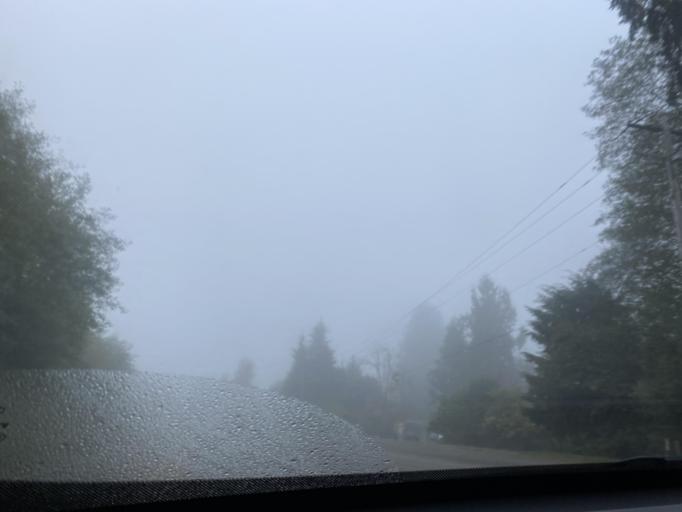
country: US
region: Washington
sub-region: Clallam County
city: Forks
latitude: 47.9317
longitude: -124.4084
